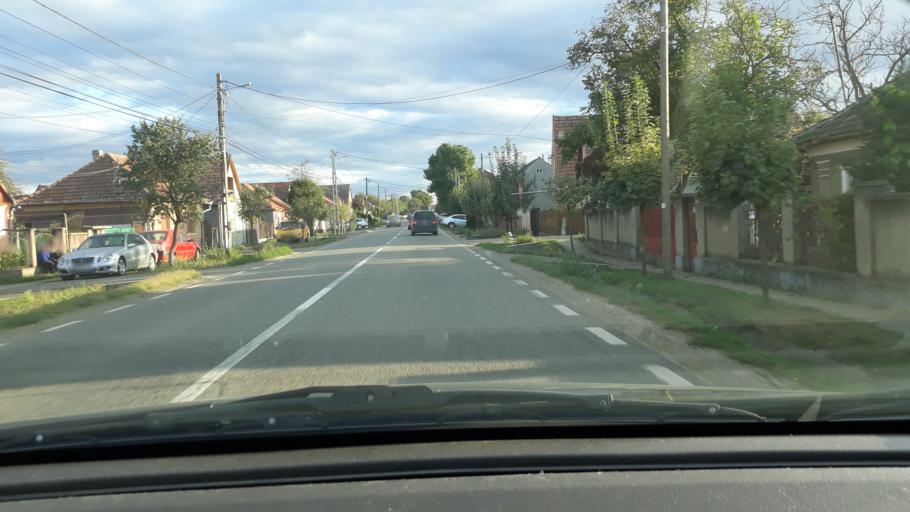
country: RO
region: Bihor
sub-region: Comuna Biharea
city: Biharea
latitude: 47.1631
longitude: 21.9222
